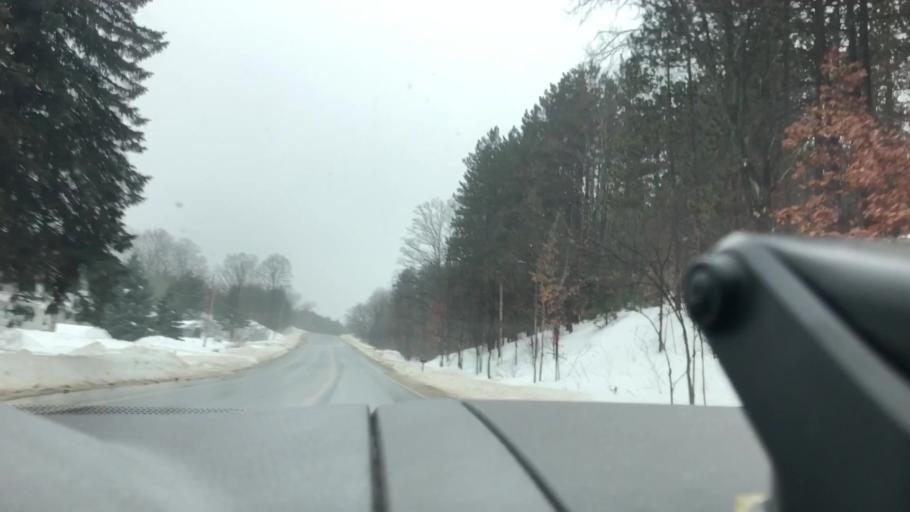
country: US
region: Michigan
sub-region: Charlevoix County
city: East Jordan
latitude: 45.1569
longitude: -85.1569
